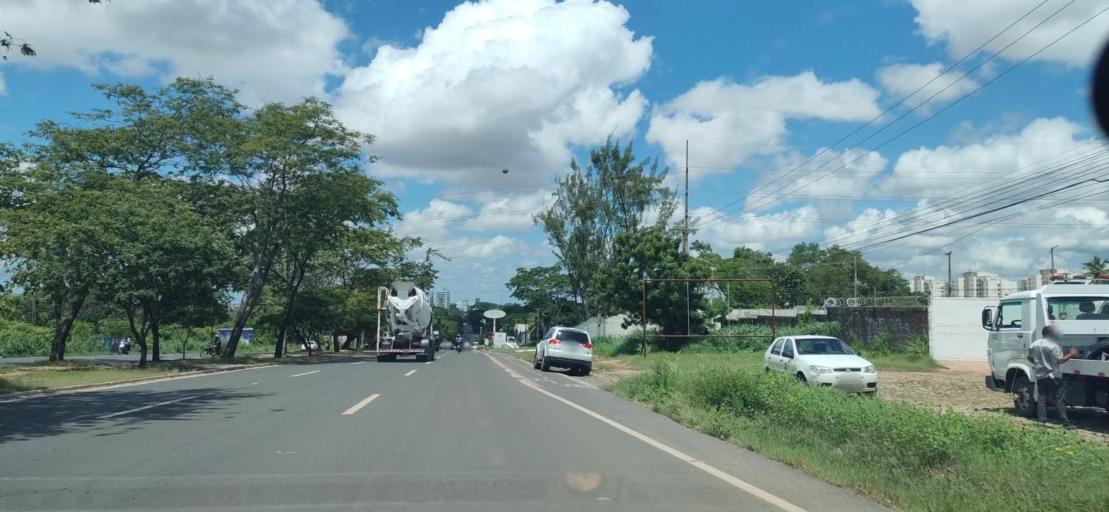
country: BR
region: Piaui
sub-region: Teresina
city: Teresina
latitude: -5.0785
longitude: -42.7507
